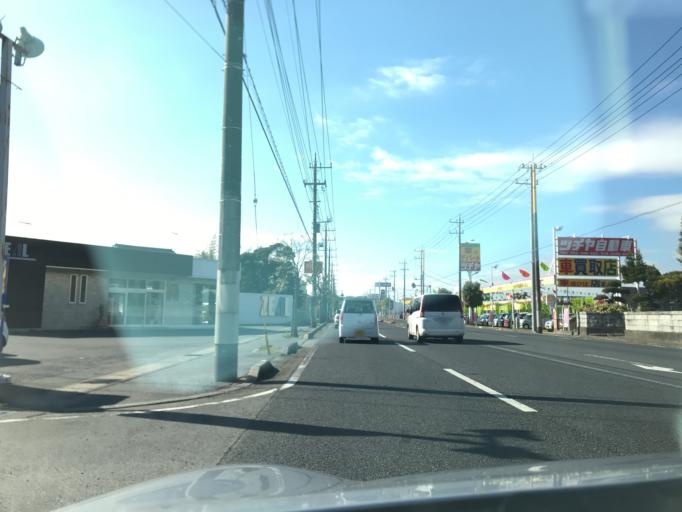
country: JP
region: Chiba
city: Mobara
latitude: 35.4432
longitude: 140.2924
